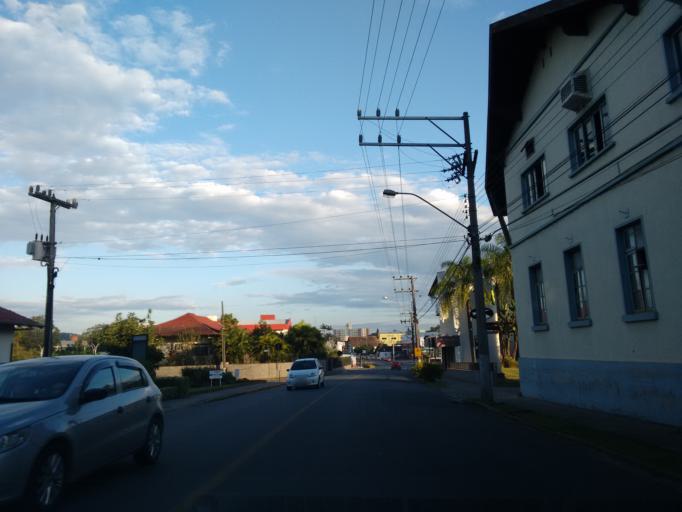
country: BR
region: Santa Catarina
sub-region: Timbo
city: Timbo
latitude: -26.8294
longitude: -49.2745
